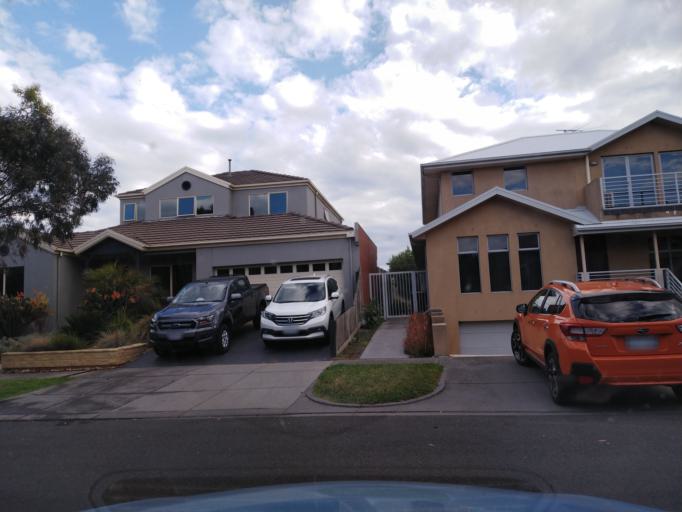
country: AU
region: Victoria
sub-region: Hobsons Bay
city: Williamstown North
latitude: -37.8613
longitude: 144.8779
